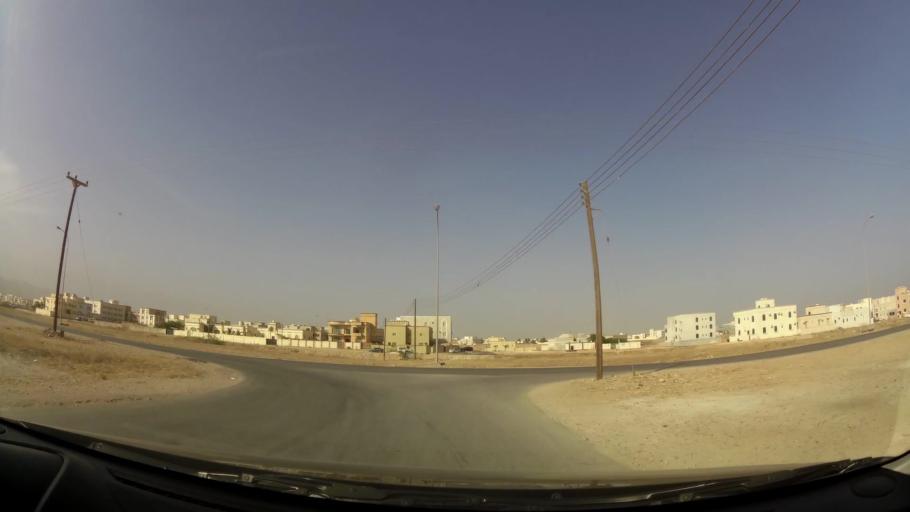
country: OM
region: Zufar
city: Salalah
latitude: 17.0059
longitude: 54.0231
